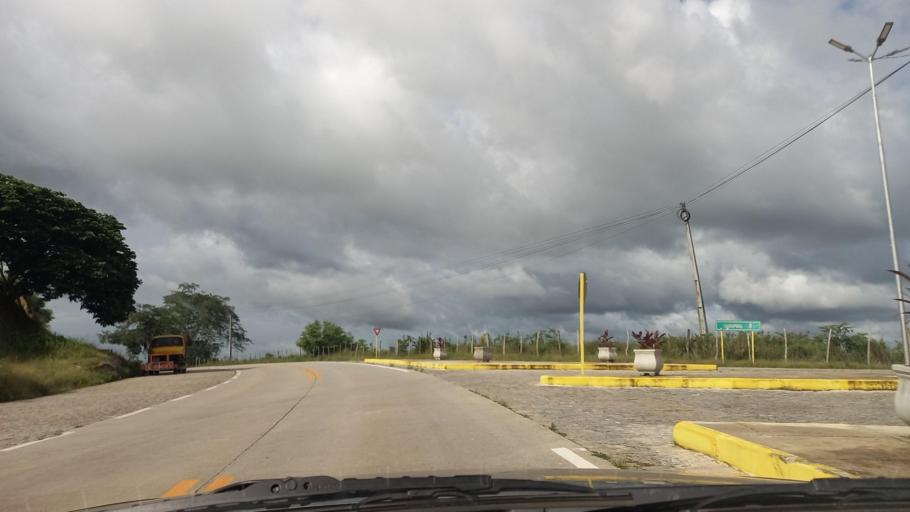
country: BR
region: Pernambuco
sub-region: Maraial
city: Maraial
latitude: -8.7901
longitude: -35.8814
